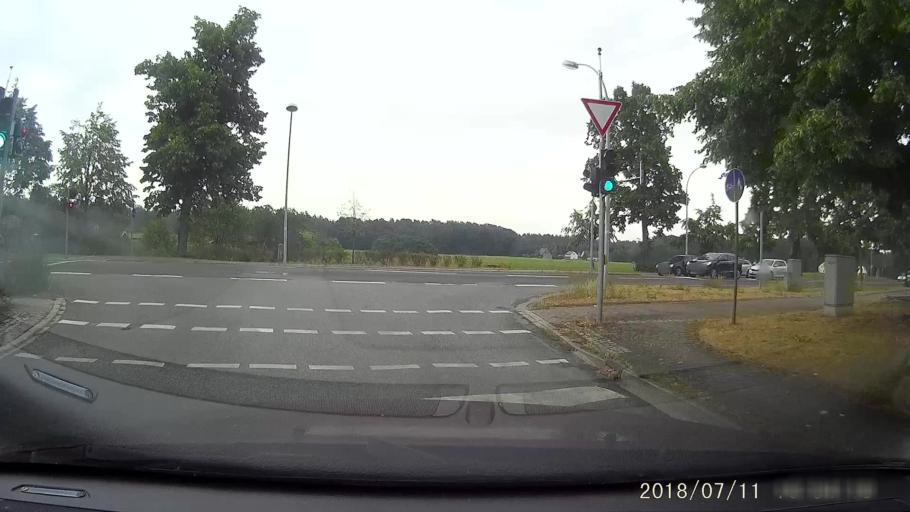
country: DE
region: Saxony
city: Niesky
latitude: 51.2860
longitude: 14.8195
